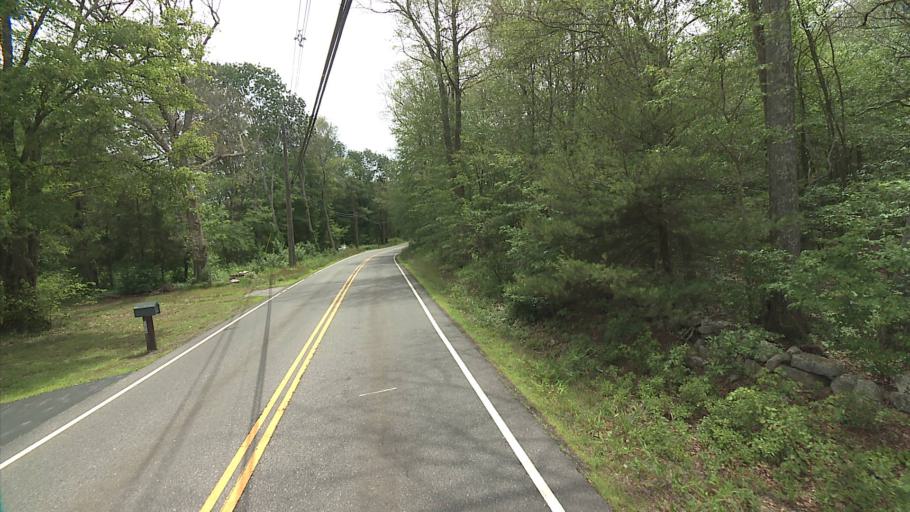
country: US
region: Connecticut
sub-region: New London County
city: Ledyard Center
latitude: 41.4477
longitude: -72.0457
